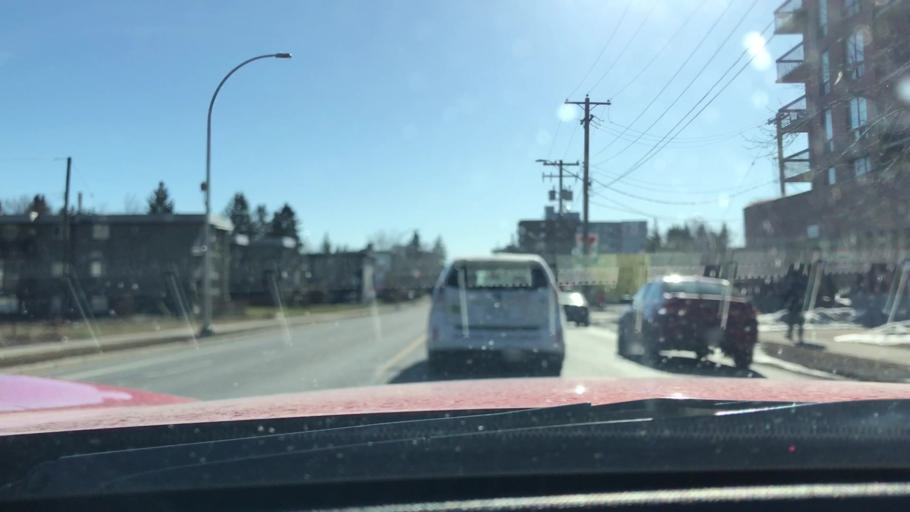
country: CA
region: Alberta
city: Calgary
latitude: 51.0378
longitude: -114.1296
